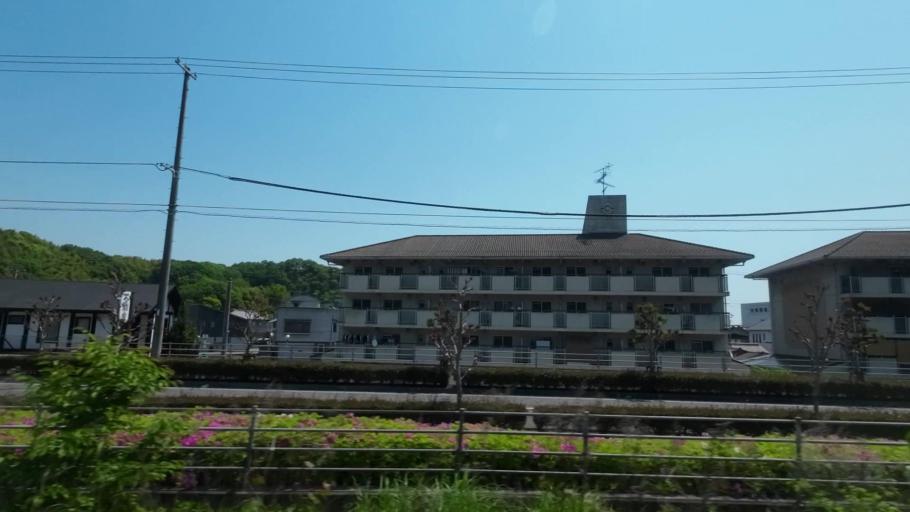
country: JP
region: Ehime
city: Hojo
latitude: 34.0868
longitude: 132.9846
